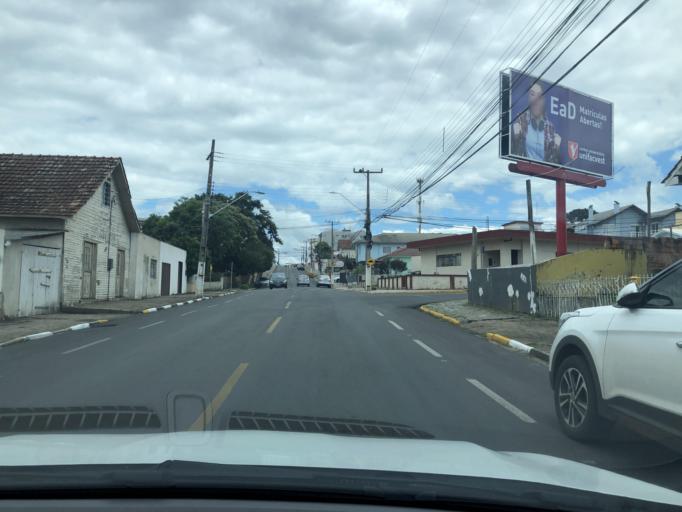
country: BR
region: Santa Catarina
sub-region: Lages
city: Lages
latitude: -27.8233
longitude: -50.3260
